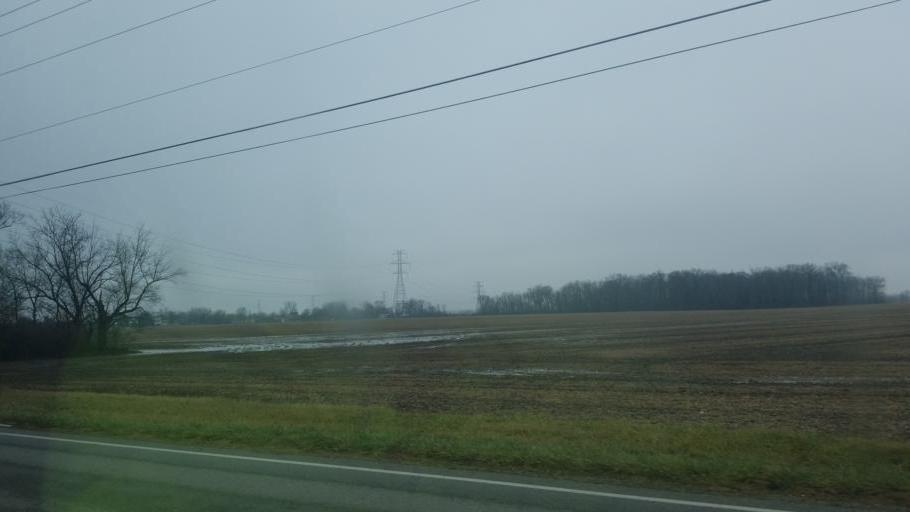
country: US
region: Ohio
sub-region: Union County
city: New California
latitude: 40.1228
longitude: -83.1937
